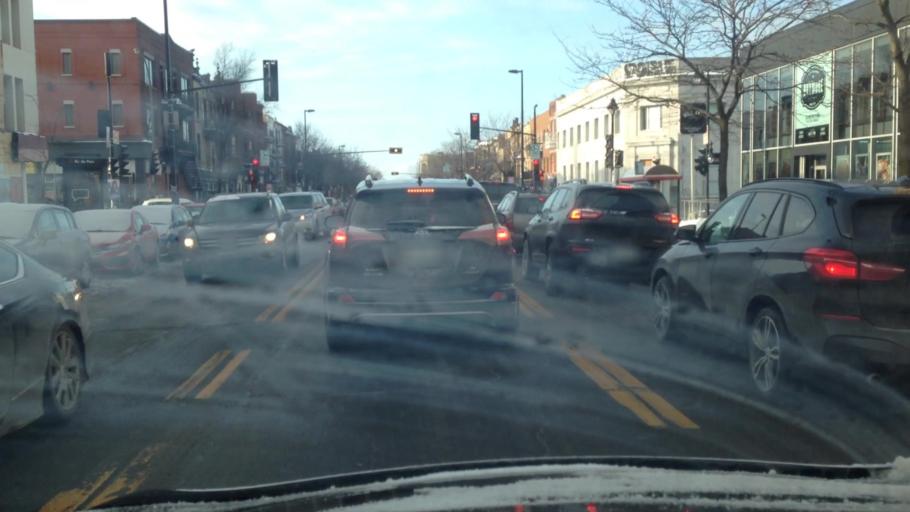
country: CA
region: Quebec
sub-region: Montreal
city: Montreal
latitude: 45.5234
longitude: -73.6049
